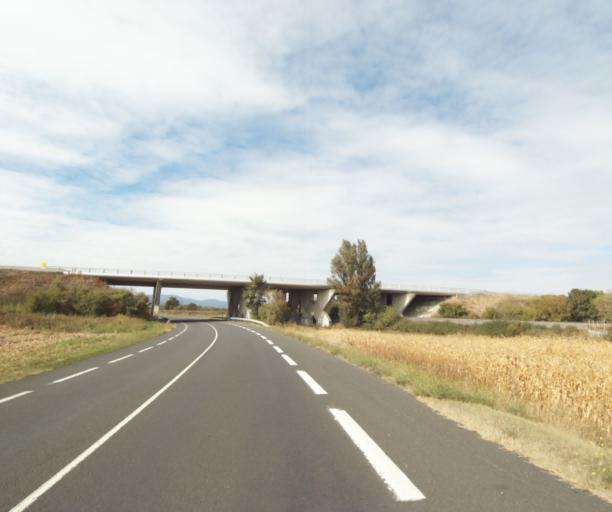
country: FR
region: Auvergne
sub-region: Departement du Puy-de-Dome
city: Malintrat
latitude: 45.7896
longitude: 3.2029
